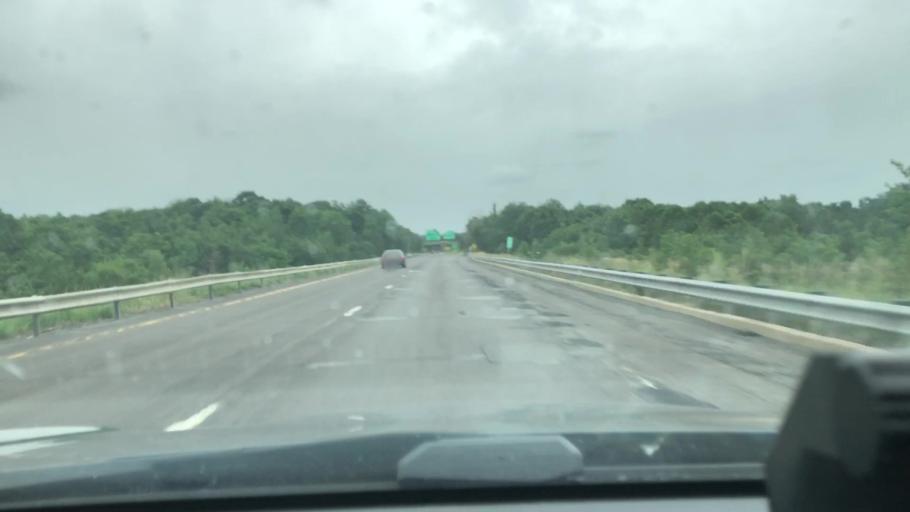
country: US
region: Pennsylvania
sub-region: Monroe County
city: Emerald Lakes
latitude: 41.0803
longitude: -75.3966
